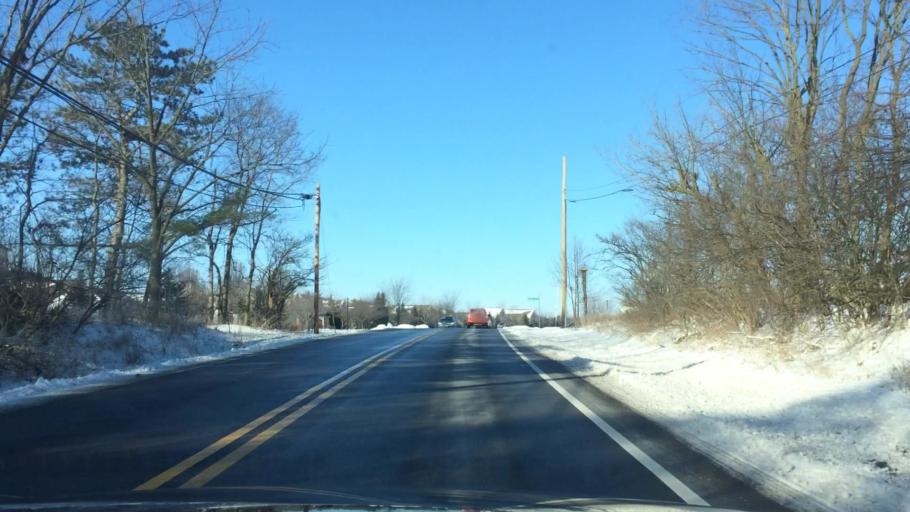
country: US
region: Ohio
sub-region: Franklin County
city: Hilliard
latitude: 40.0551
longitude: -83.1678
